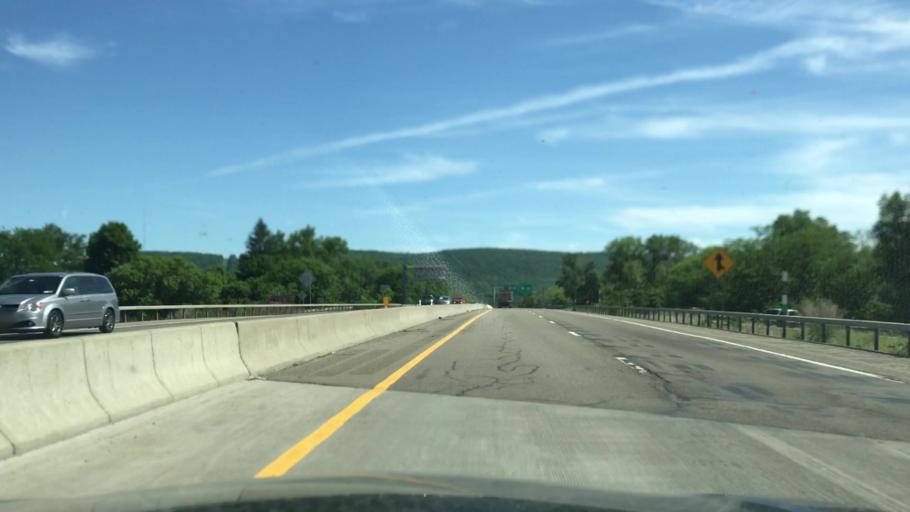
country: US
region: New York
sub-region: Steuben County
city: Painted Post
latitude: 42.1704
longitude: -77.1047
